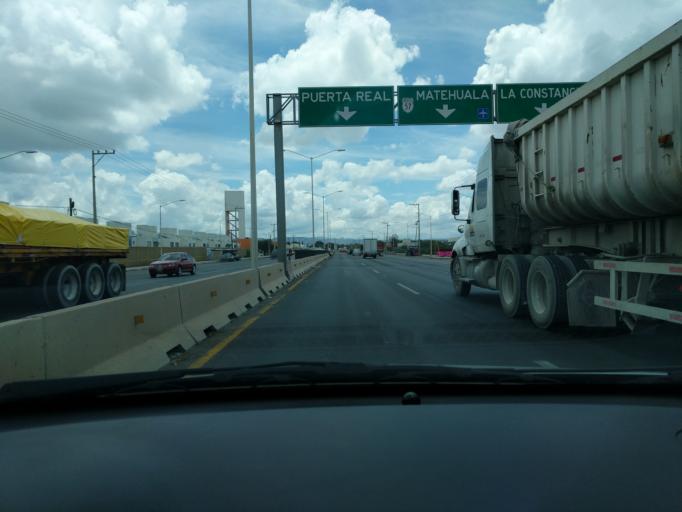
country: MX
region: San Luis Potosi
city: Soledad Diez Gutierrez
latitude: 22.2136
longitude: -100.9399
